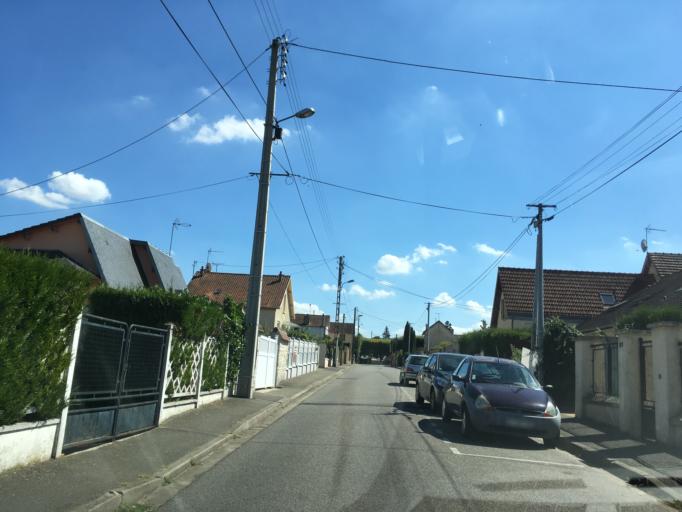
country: FR
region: Haute-Normandie
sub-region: Departement de l'Eure
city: Vernon
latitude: 49.0906
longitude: 1.4661
